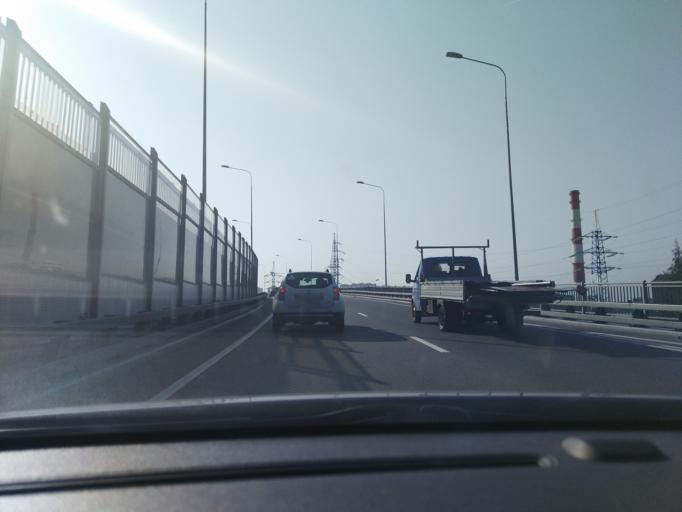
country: RU
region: St.-Petersburg
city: Kupchino
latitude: 59.8318
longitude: 30.3104
